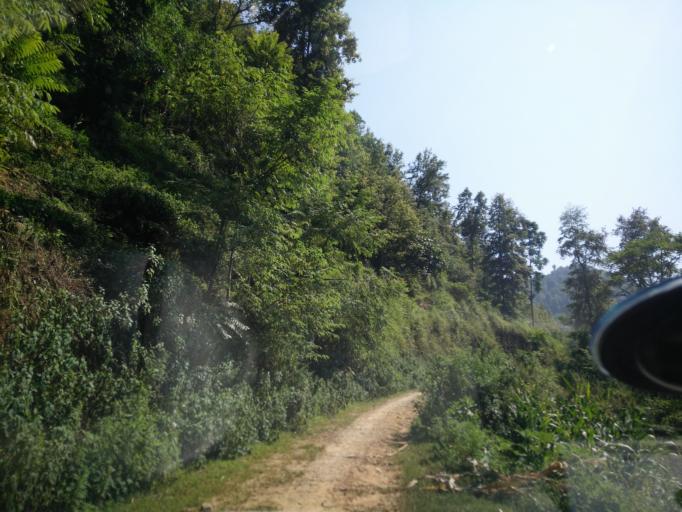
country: CN
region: Guangxi Zhuangzu Zizhiqu
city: Xinzhou
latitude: 25.1846
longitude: 105.6898
